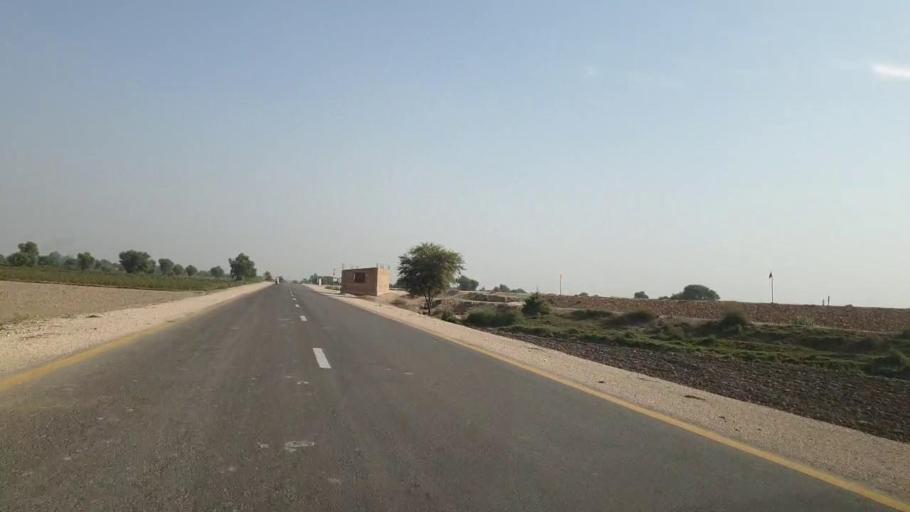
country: PK
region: Sindh
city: Sehwan
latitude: 26.4558
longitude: 67.8076
